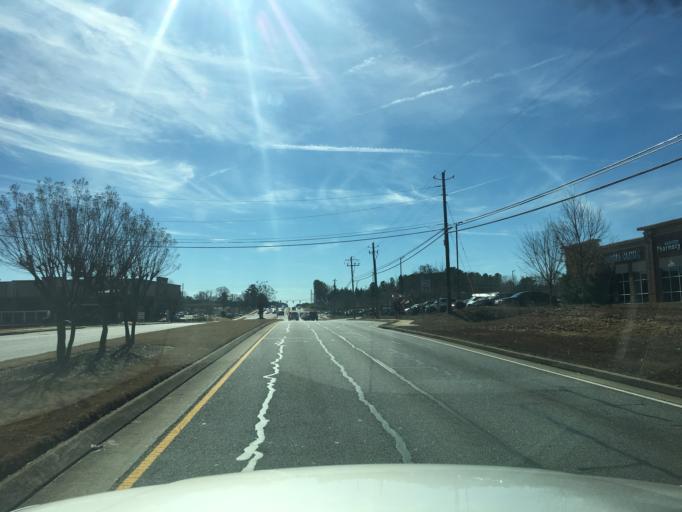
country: US
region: Georgia
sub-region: Gwinnett County
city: Lawrenceville
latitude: 33.9198
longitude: -83.9994
